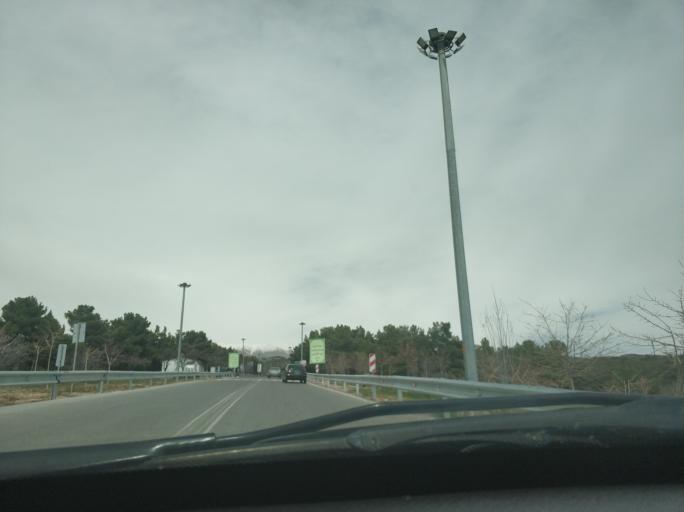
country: IR
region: Tehran
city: Tajrish
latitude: 35.7739
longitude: 51.5517
